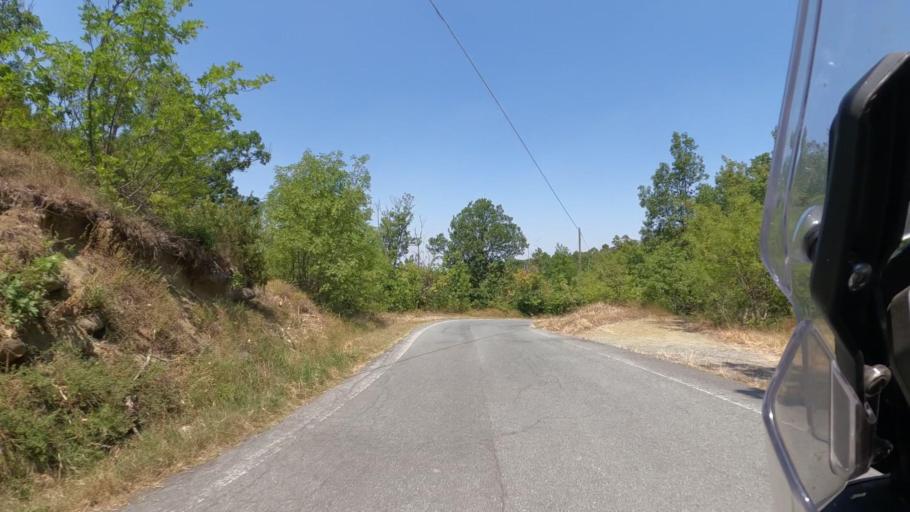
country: IT
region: Piedmont
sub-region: Provincia di Alessandria
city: Morbello
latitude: 44.5688
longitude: 8.5180
